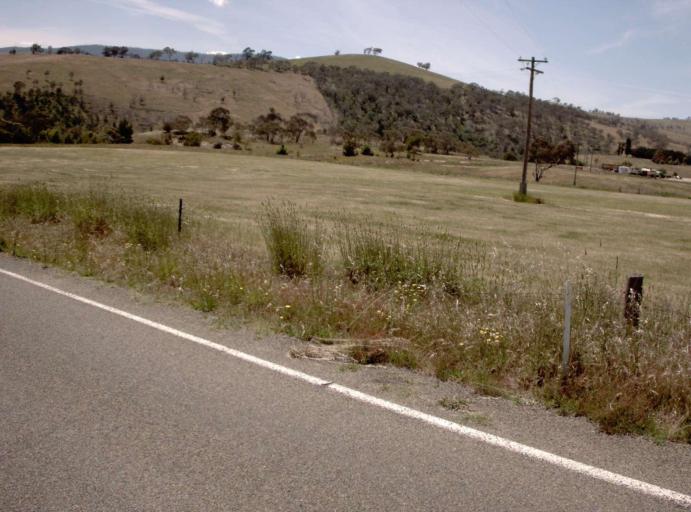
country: AU
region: Victoria
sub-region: Alpine
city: Mount Beauty
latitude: -37.1137
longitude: 147.5719
